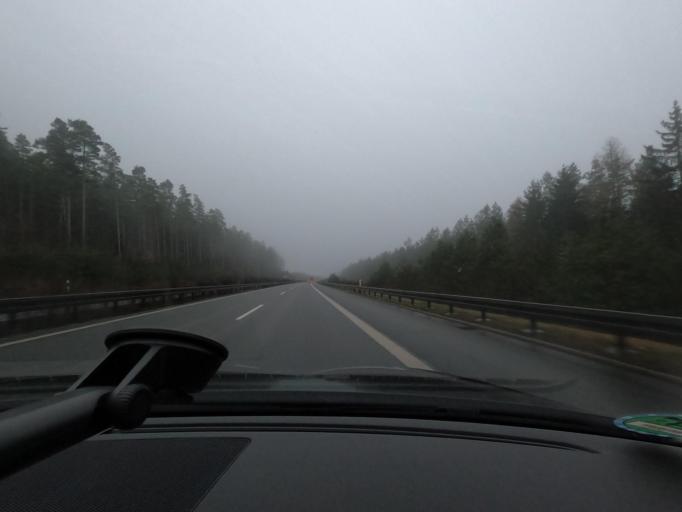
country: DE
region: Thuringia
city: Behringen
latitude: 50.7285
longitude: 10.9816
